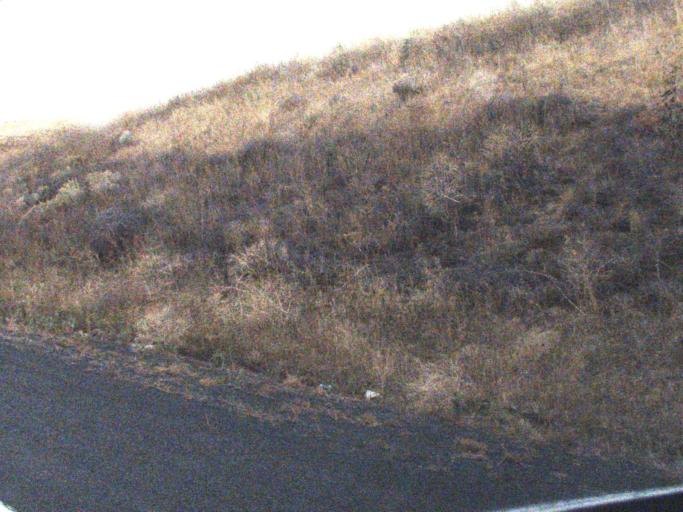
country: US
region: Washington
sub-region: Adams County
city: Ritzville
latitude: 46.7657
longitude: -118.3374
